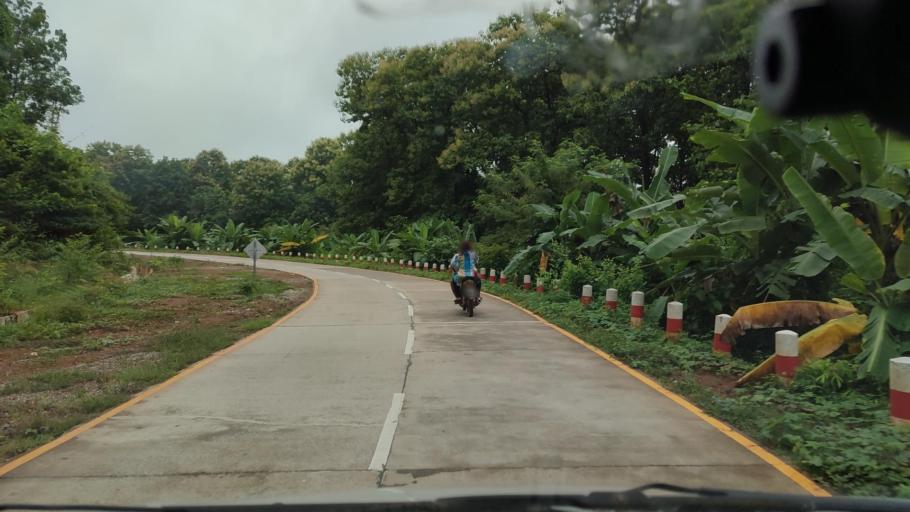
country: MM
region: Bago
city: Taungoo
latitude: 18.9998
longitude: 96.5297
